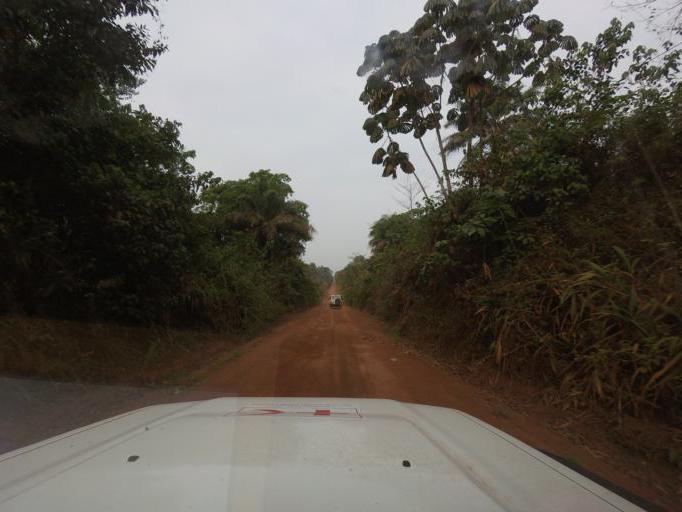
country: LR
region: Lofa
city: Voinjama
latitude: 8.3800
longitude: -9.8413
